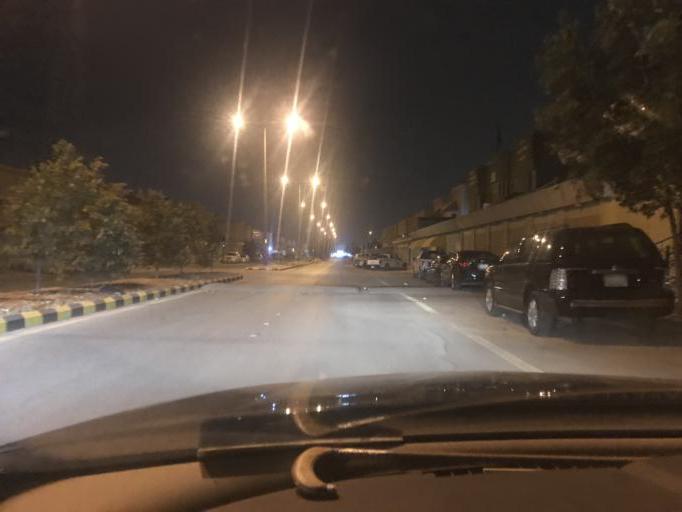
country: SA
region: Ar Riyad
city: Riyadh
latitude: 24.7528
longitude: 46.7775
